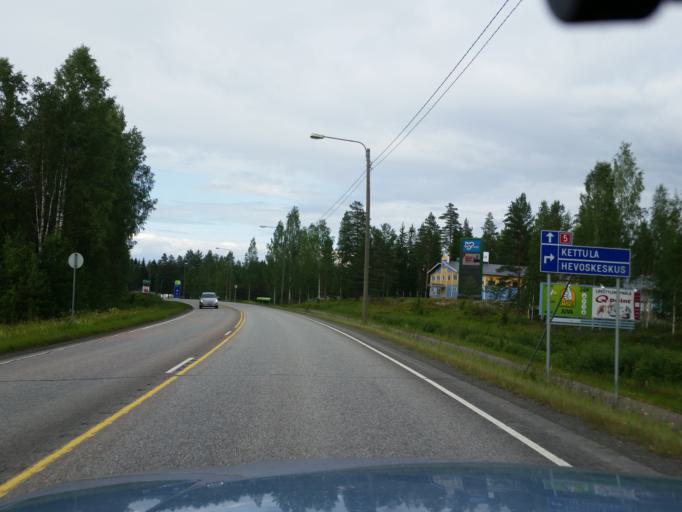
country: FI
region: Southern Savonia
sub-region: Pieksaemaeki
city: Juva
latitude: 61.8868
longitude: 27.7934
